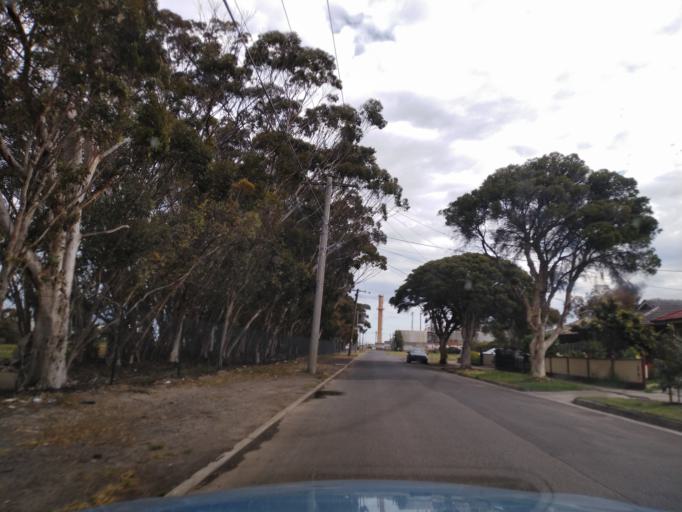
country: AU
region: Victoria
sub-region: Hobsons Bay
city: Altona North
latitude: -37.8451
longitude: 144.8541
